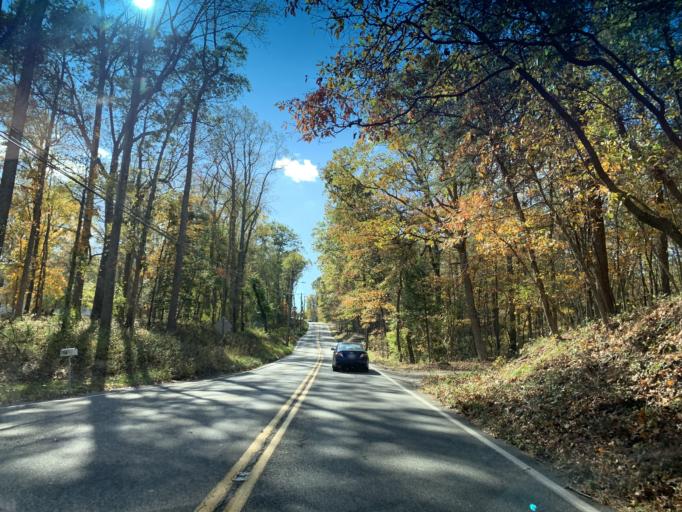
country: US
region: Maryland
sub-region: Anne Arundel County
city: Gambrills
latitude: 39.0891
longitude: -76.6543
